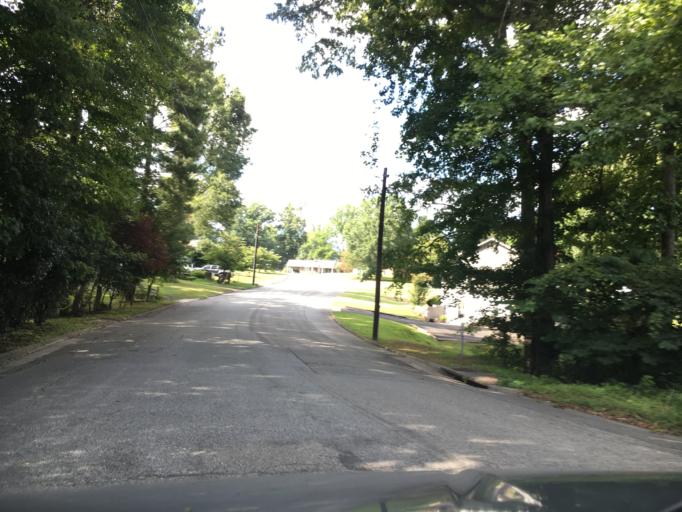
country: US
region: Virginia
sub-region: Halifax County
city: South Boston
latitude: 36.7109
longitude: -78.9097
